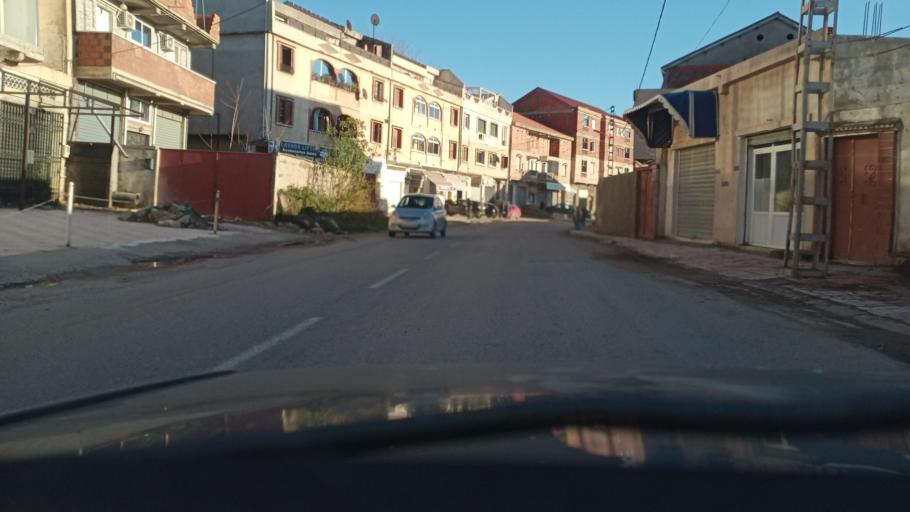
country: DZ
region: Tizi Ouzou
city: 'Ain el Hammam
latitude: 36.5628
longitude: 4.3236
